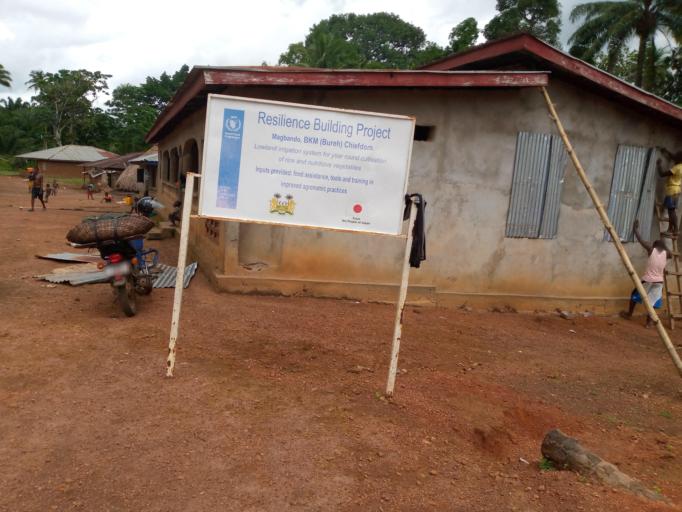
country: SL
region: Northern Province
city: Mange
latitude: 8.9776
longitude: -12.7086
